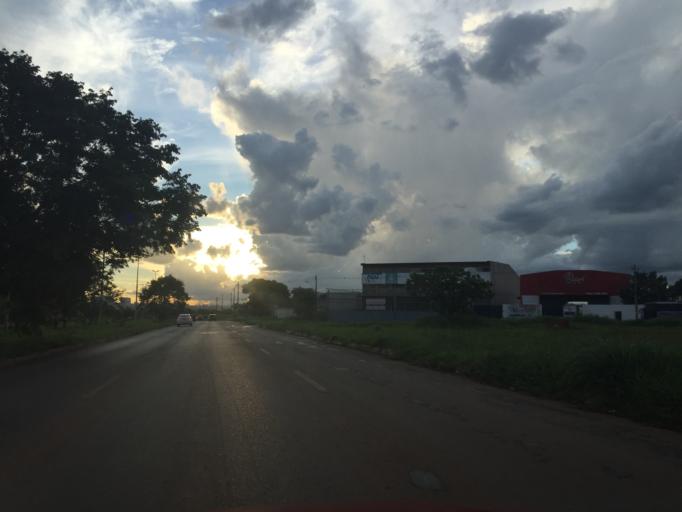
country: BR
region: Federal District
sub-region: Brasilia
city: Brasilia
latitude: -15.7940
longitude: -47.9884
